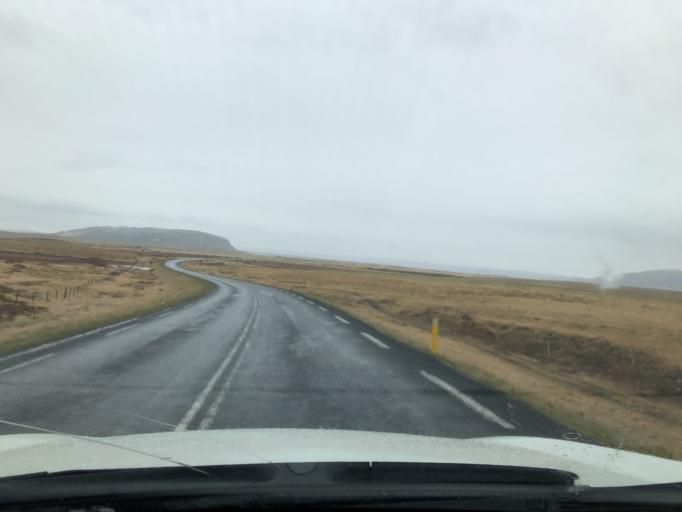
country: IS
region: South
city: Selfoss
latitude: 64.1066
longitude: -20.6988
